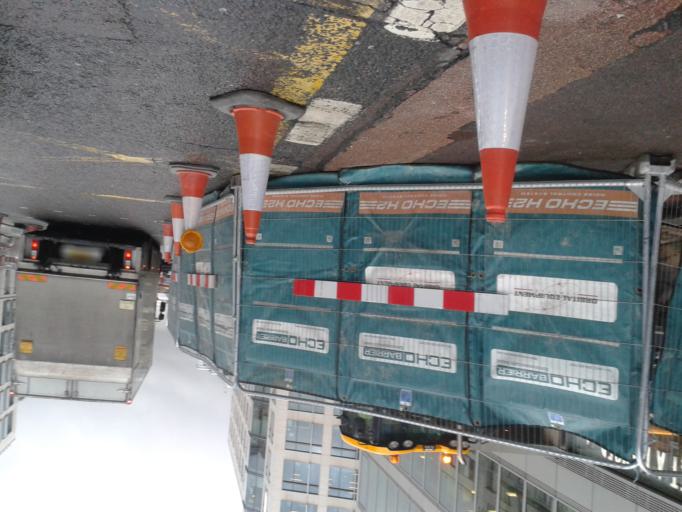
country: GB
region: England
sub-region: Greater London
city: Clerkenwell
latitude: 51.5159
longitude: -0.1046
